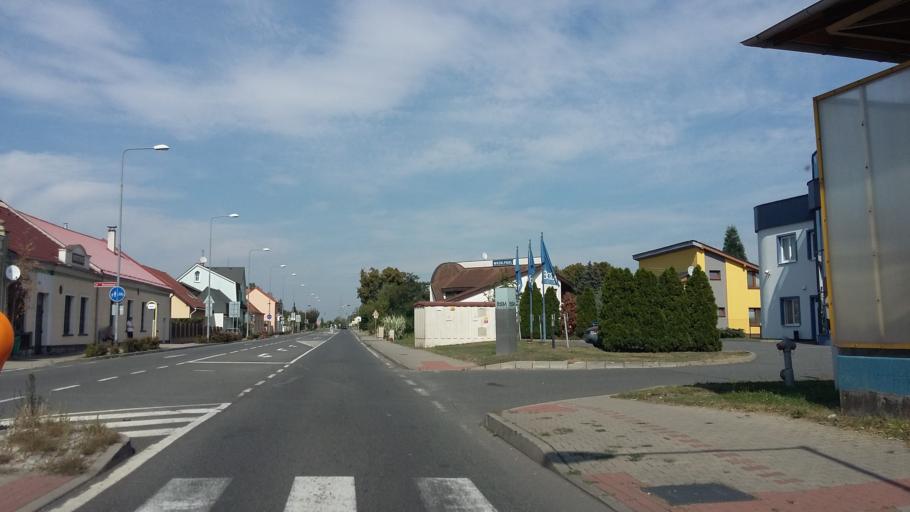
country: CZ
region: Central Bohemia
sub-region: Okres Kolin
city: Kolin
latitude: 50.0474
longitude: 15.2188
